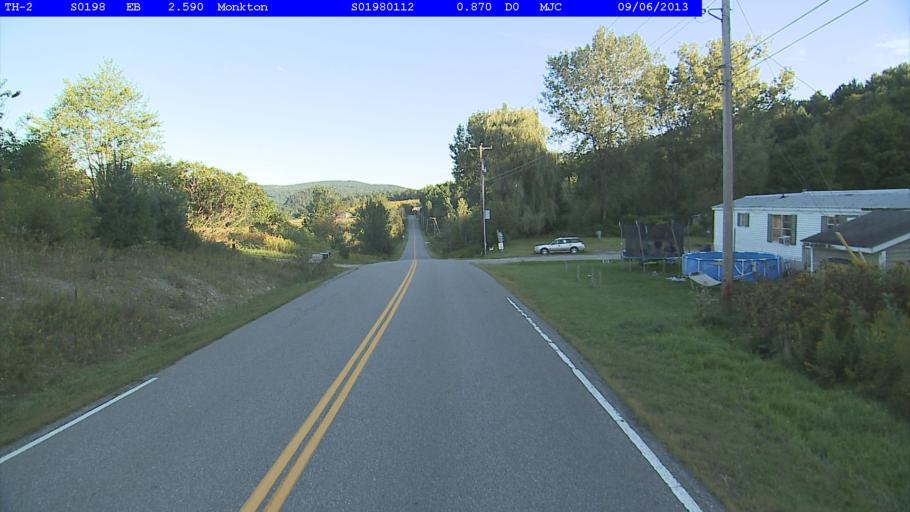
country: US
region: Vermont
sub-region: Chittenden County
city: Hinesburg
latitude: 44.2528
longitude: -73.1788
